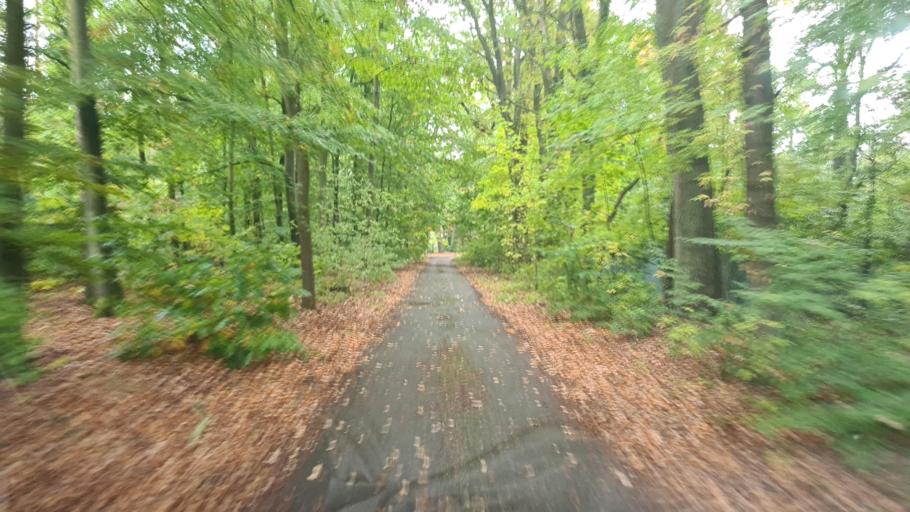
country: DE
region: Brandenburg
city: Storkow
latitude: 52.2237
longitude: 13.9348
